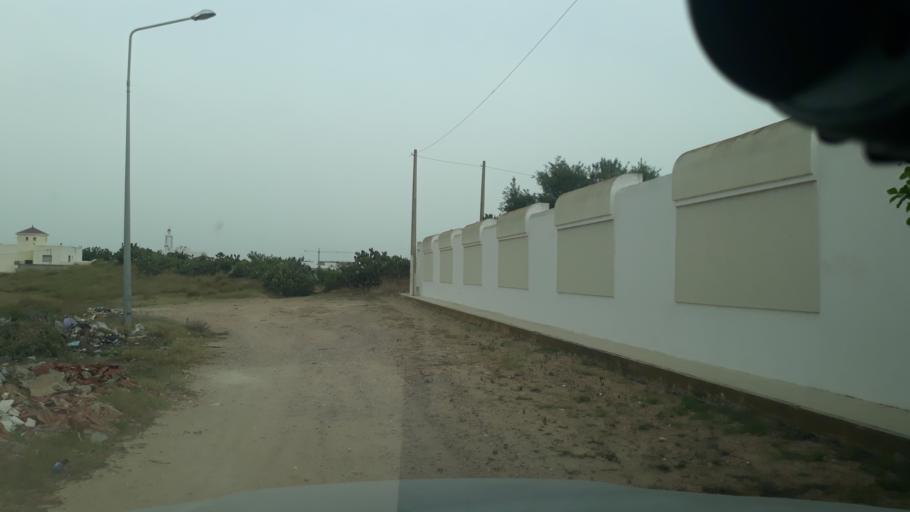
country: TN
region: Safaqis
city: Al Qarmadah
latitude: 34.7828
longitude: 10.7725
